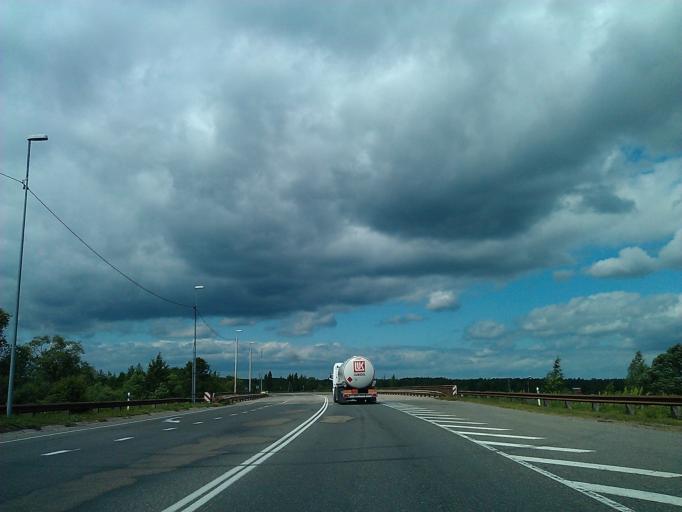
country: LV
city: Tireli
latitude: 56.9316
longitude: 23.6070
